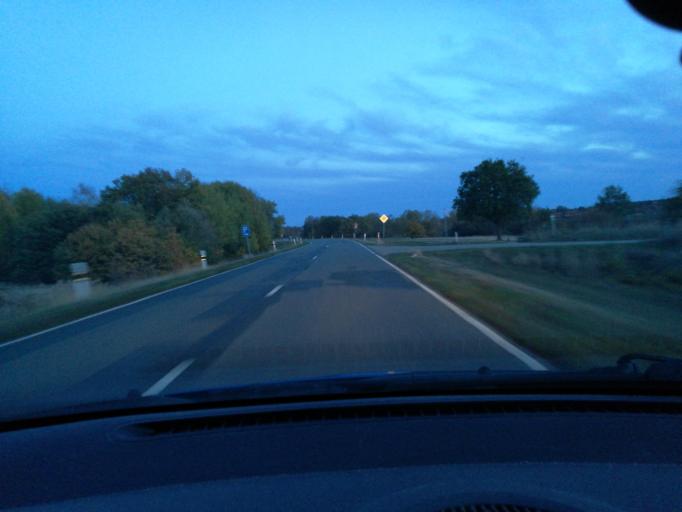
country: DE
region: Lower Saxony
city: Gartow
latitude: 53.0325
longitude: 11.4586
